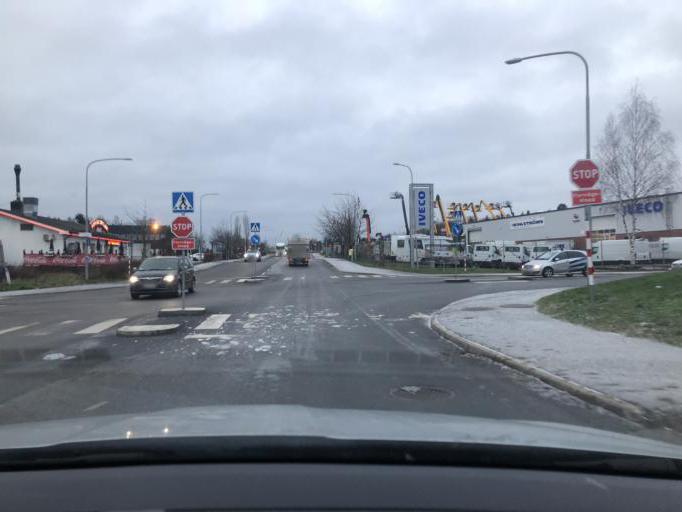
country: SE
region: Stockholm
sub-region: Jarfalla Kommun
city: Jakobsberg
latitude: 59.3896
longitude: 17.8789
